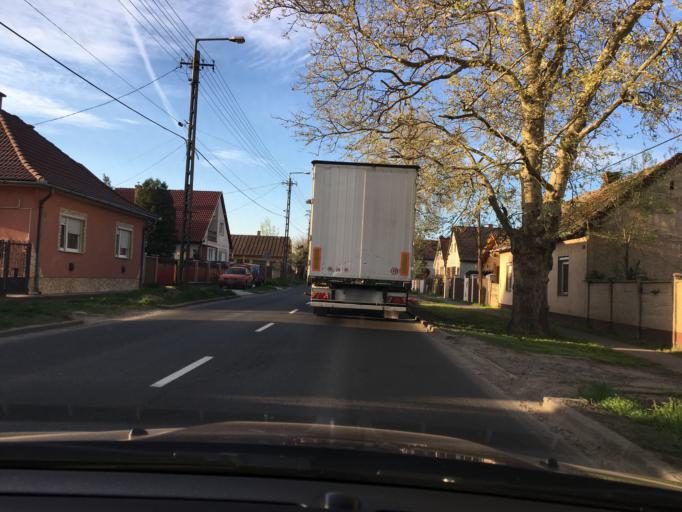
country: HU
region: Hajdu-Bihar
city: Mikepercs
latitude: 47.4443
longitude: 21.6319
